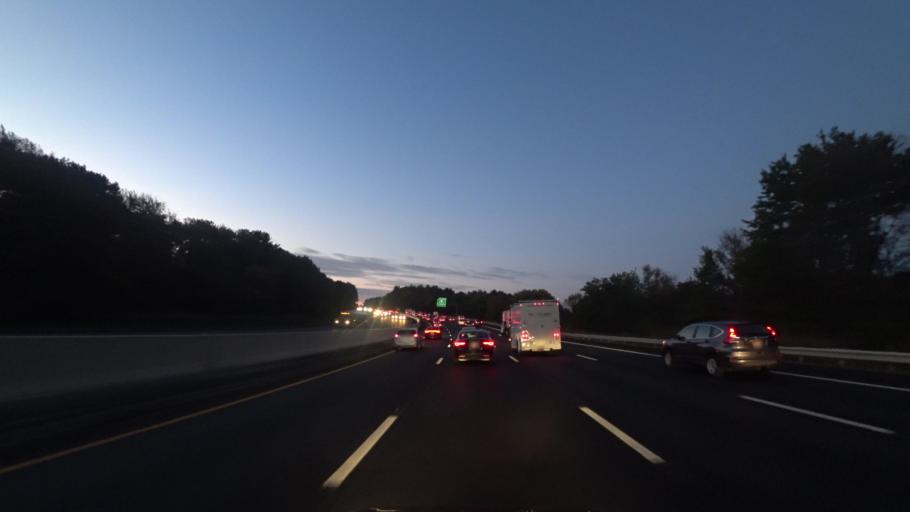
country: US
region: Massachusetts
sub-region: Middlesex County
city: Bedford
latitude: 42.4587
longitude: -71.2591
